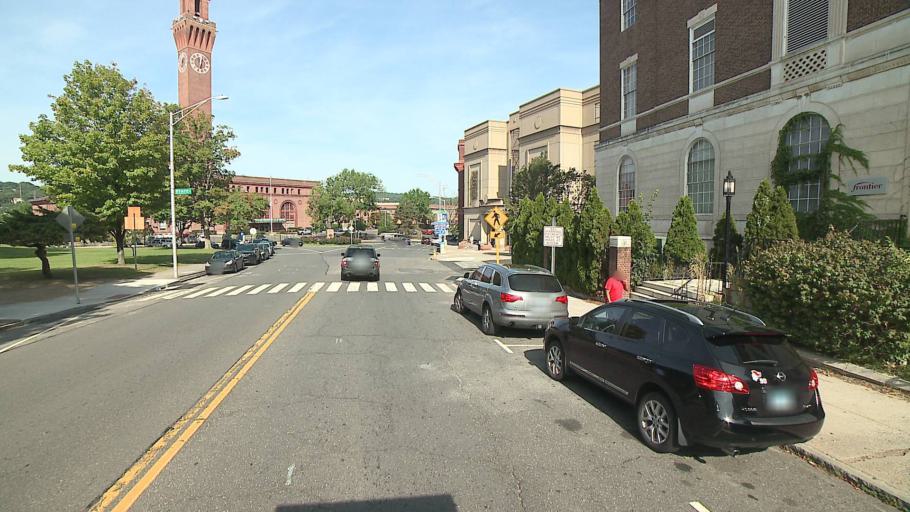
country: US
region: Connecticut
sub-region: New Haven County
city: Waterbury
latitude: 41.5550
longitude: -73.0453
